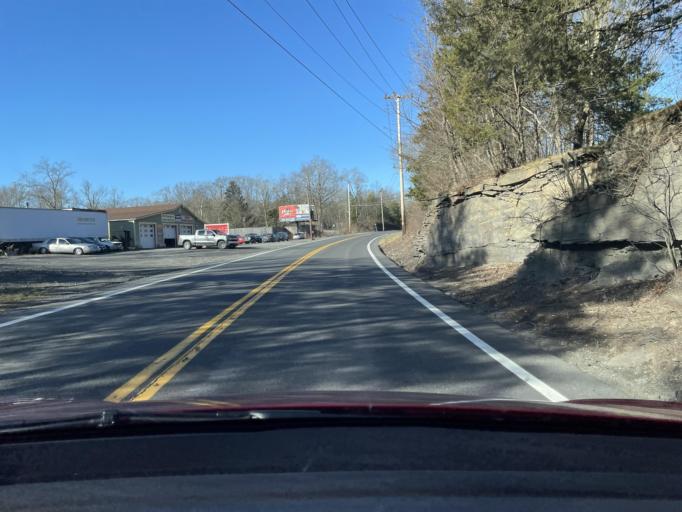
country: US
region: New York
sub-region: Ulster County
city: Manorville
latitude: 42.0733
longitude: -74.0292
